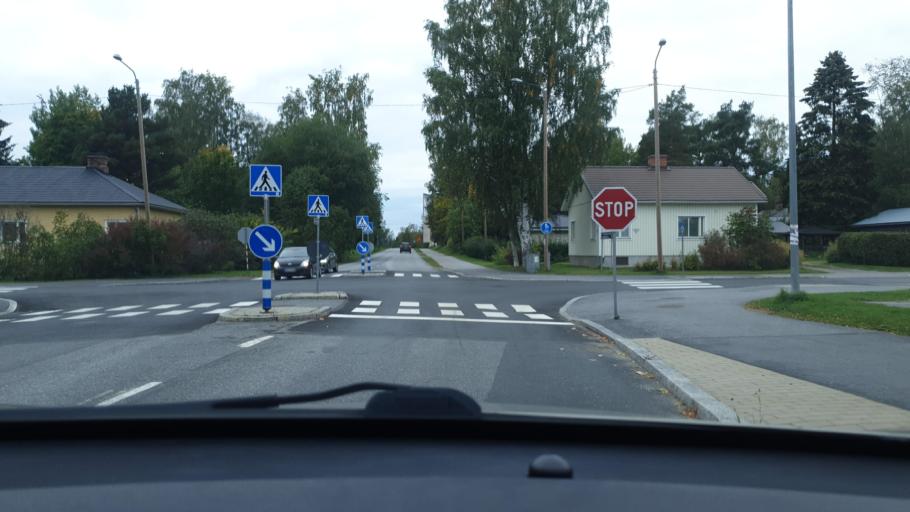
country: FI
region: Ostrobothnia
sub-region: Vaasa
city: Korsholm
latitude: 63.0950
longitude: 21.6673
